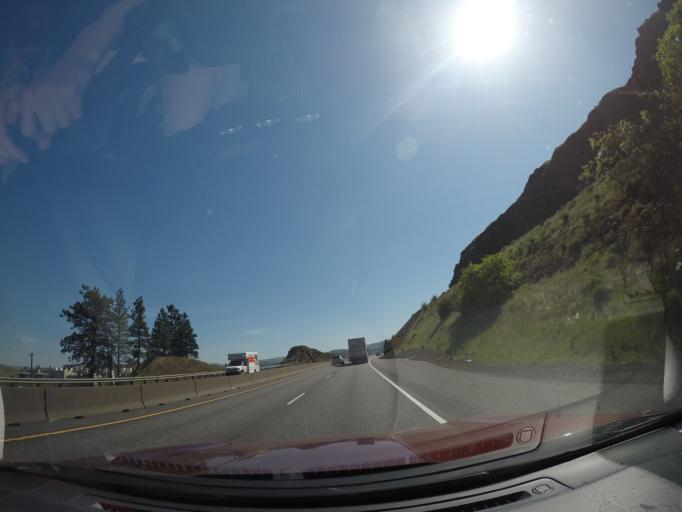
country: US
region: Oregon
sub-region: Wasco County
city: Chenoweth
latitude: 45.6415
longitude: -121.2090
